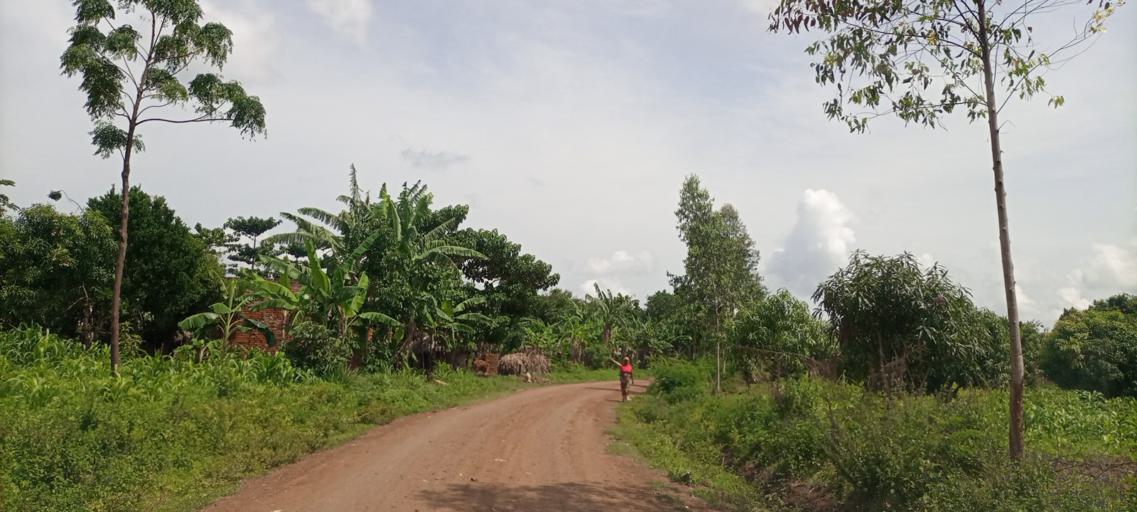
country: UG
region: Eastern Region
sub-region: Budaka District
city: Budaka
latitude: 1.1688
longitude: 33.9418
